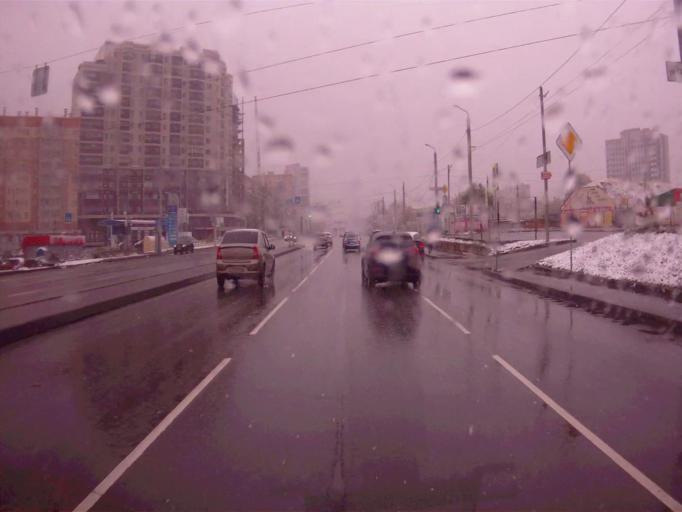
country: RU
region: Chelyabinsk
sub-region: Gorod Chelyabinsk
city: Chelyabinsk
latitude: 55.1449
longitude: 61.4026
